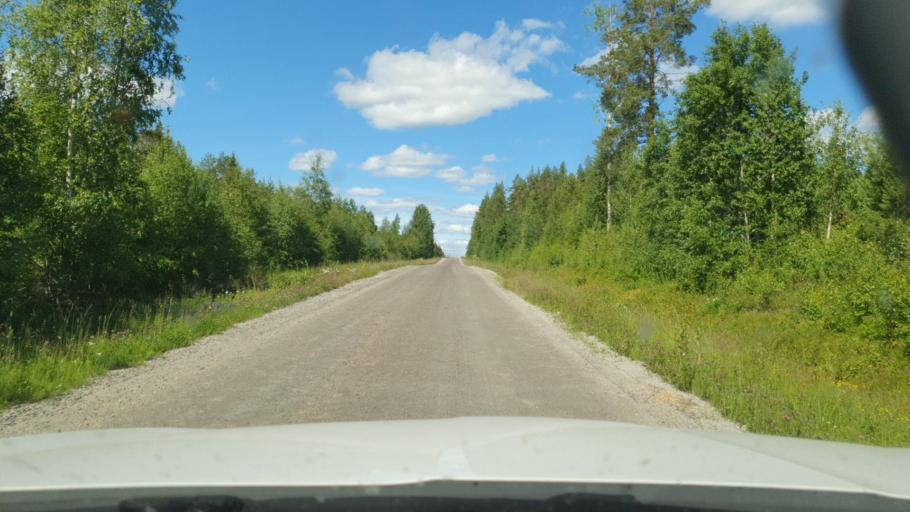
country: SE
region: Vaesterbotten
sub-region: Skelleftea Kommun
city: Backa
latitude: 65.1433
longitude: 21.1740
